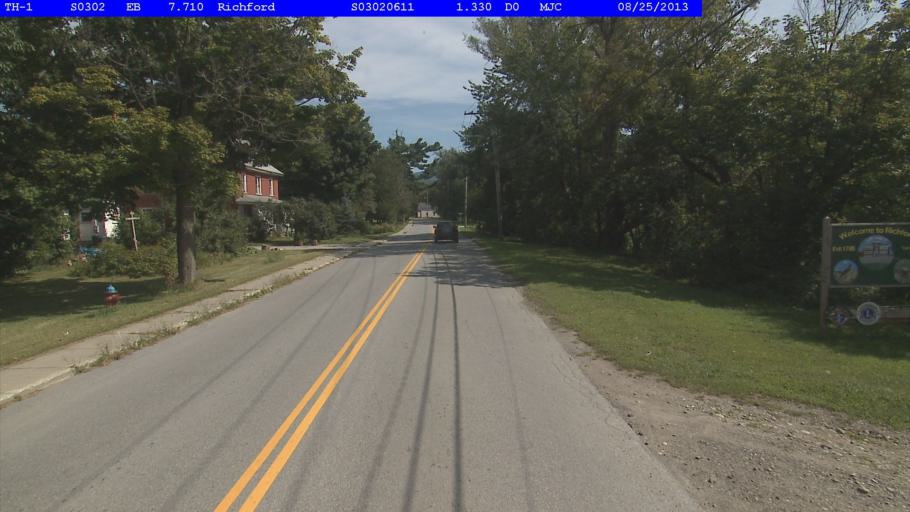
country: US
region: Vermont
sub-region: Franklin County
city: Richford
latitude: 44.9991
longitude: -72.6769
